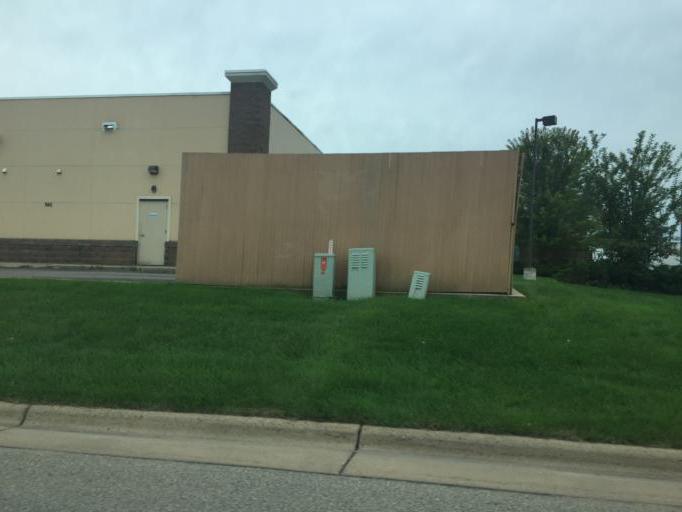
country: US
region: Minnesota
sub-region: Winona County
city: Winona
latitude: 44.0352
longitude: -91.6191
